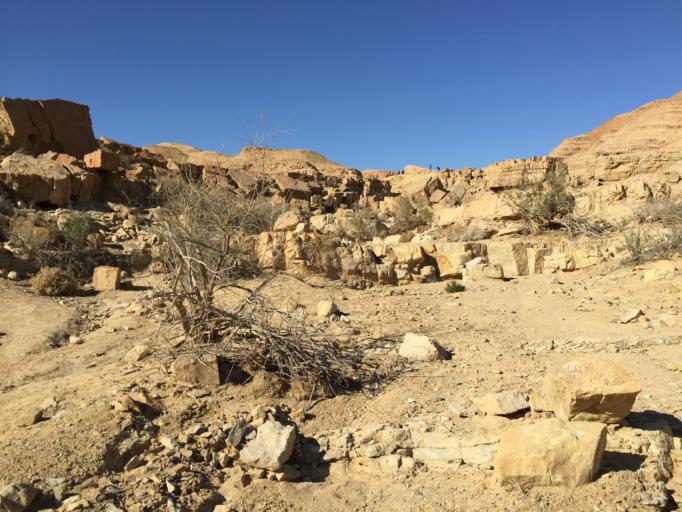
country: IL
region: Southern District
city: Mitzpe Ramon
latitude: 30.6036
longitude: 34.9485
